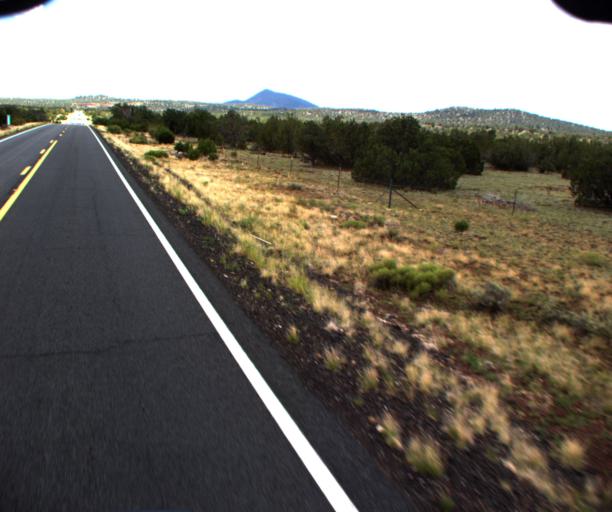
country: US
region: Arizona
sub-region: Coconino County
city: Parks
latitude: 35.5717
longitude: -111.9257
